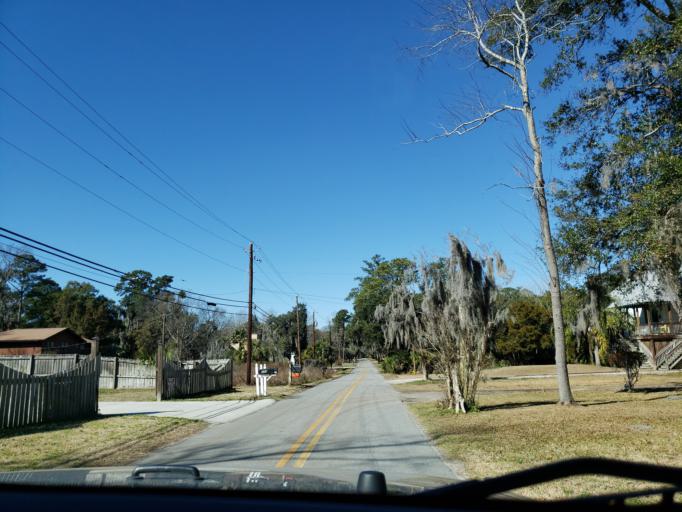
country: US
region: Georgia
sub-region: Chatham County
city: Whitemarsh Island
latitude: 32.0404
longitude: -80.9910
